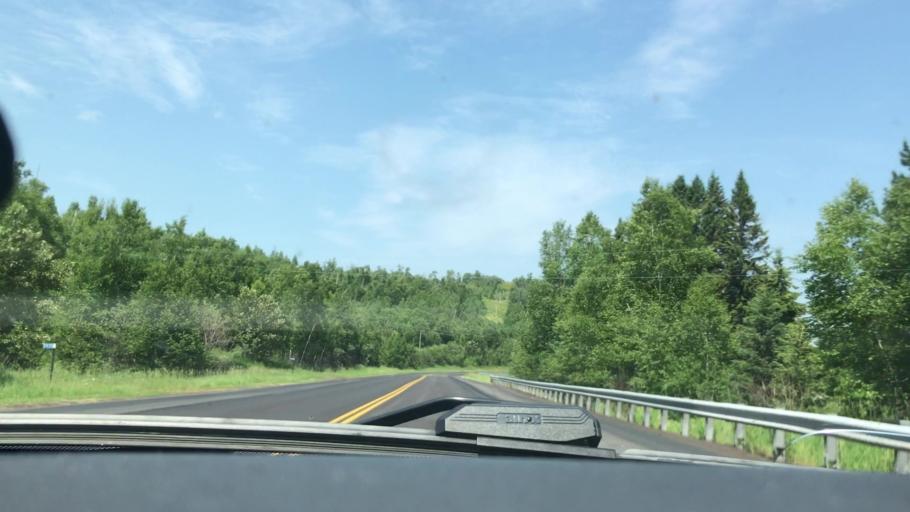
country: US
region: Minnesota
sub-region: Lake County
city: Silver Bay
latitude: 47.3642
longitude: -91.1729
